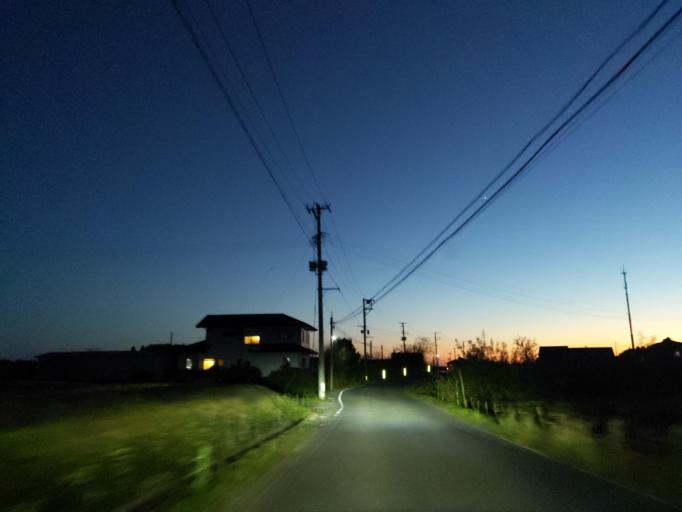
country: JP
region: Fukushima
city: Sukagawa
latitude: 37.3193
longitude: 140.3910
